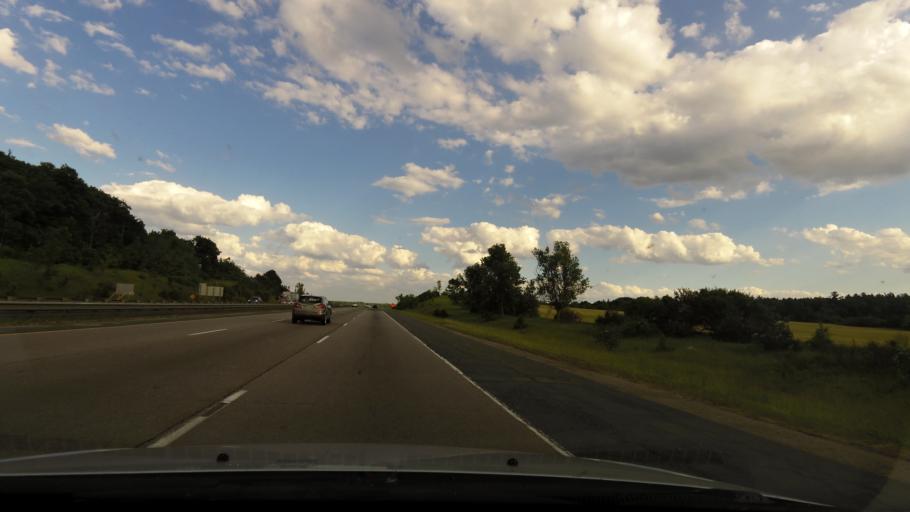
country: CA
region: Ontario
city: Bradford West Gwillimbury
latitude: 44.0580
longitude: -79.6143
